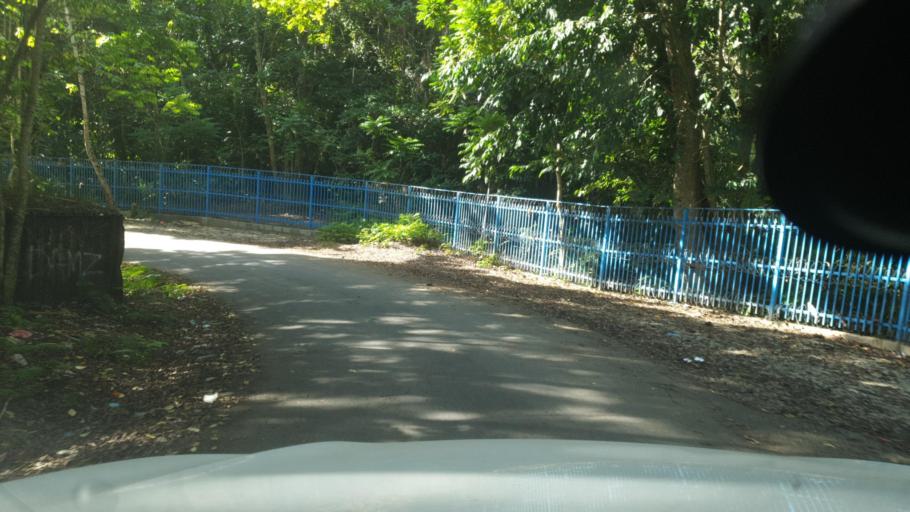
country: SB
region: Guadalcanal
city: Honiara
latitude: -9.4392
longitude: 159.9397
